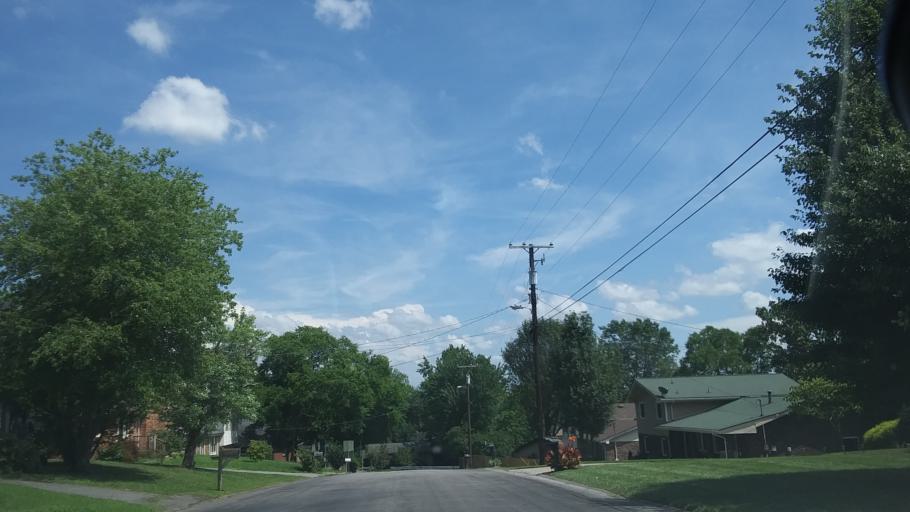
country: US
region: Tennessee
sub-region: Rutherford County
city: La Vergne
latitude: 36.0816
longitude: -86.6336
